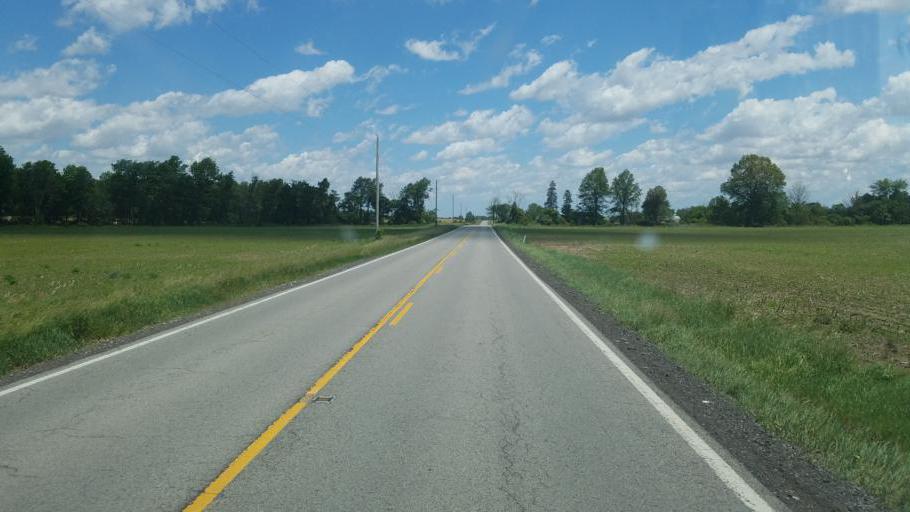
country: US
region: Ohio
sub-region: Huron County
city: Plymouth
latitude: 40.9543
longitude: -82.7198
